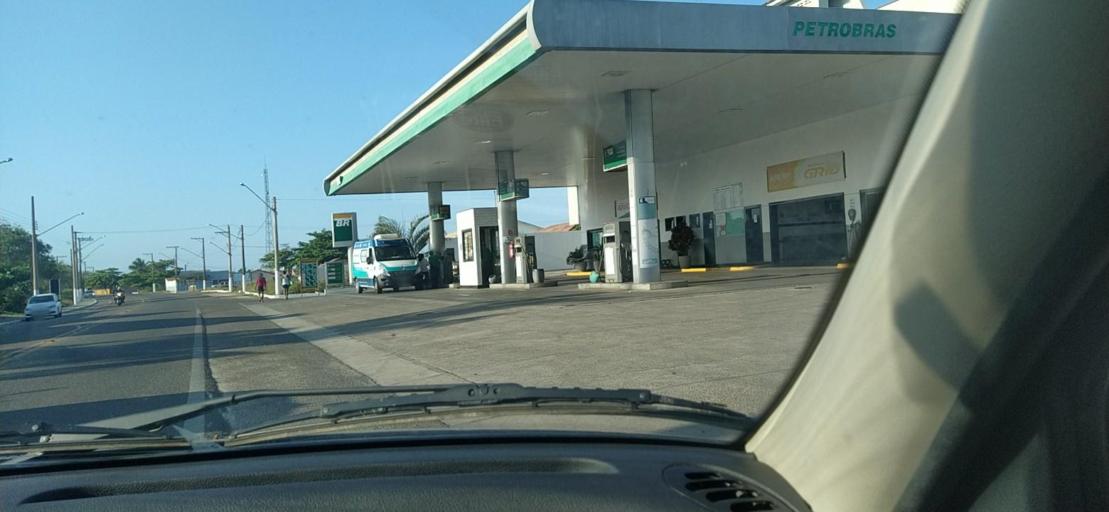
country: BR
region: Espirito Santo
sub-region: Conceicao Da Barra
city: Conceicao da Barra
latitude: -18.5790
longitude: -39.7327
